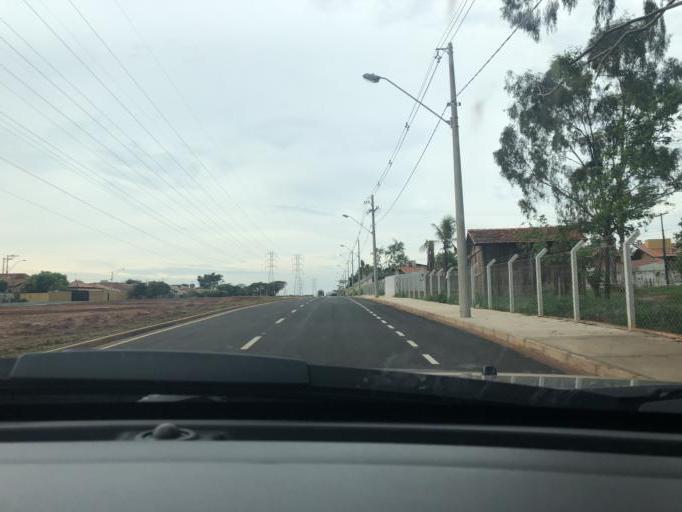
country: BR
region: Sao Paulo
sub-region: Sao Jose Do Rio Preto
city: Sao Jose do Rio Preto
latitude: -20.8441
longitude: -49.4061
